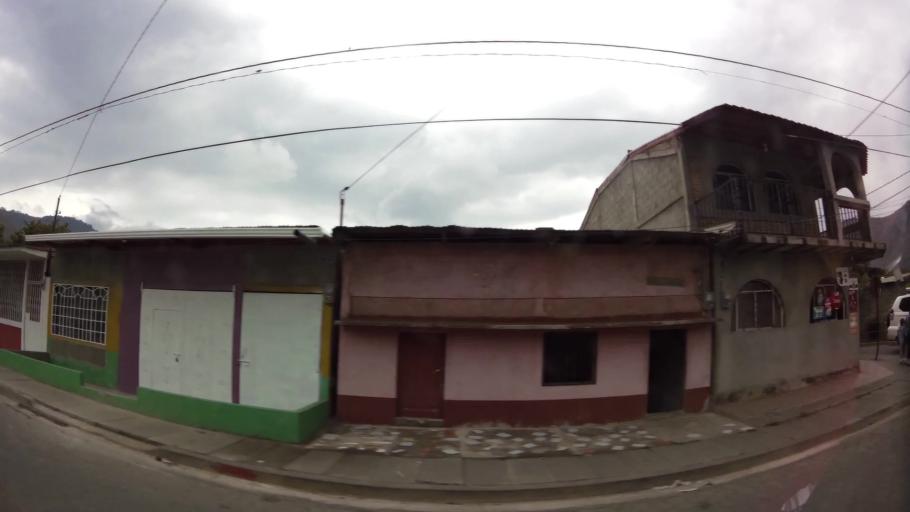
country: NI
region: Jinotega
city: Jinotega
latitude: 13.0977
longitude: -86.0009
